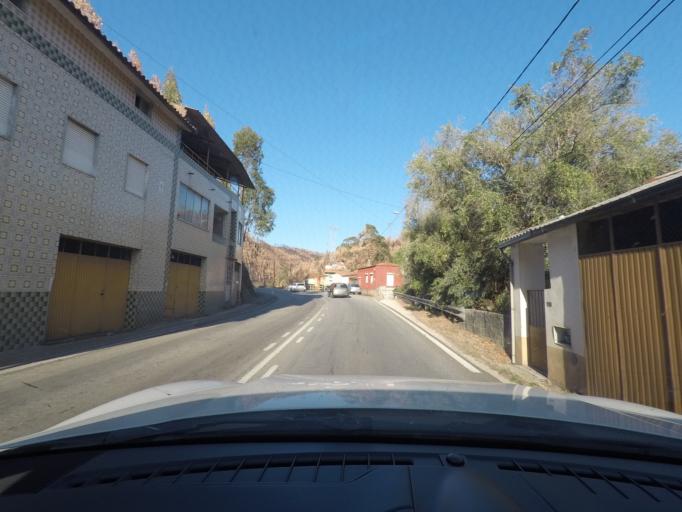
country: PT
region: Coimbra
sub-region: Coimbra
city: Coimbra
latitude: 40.1801
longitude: -8.3686
